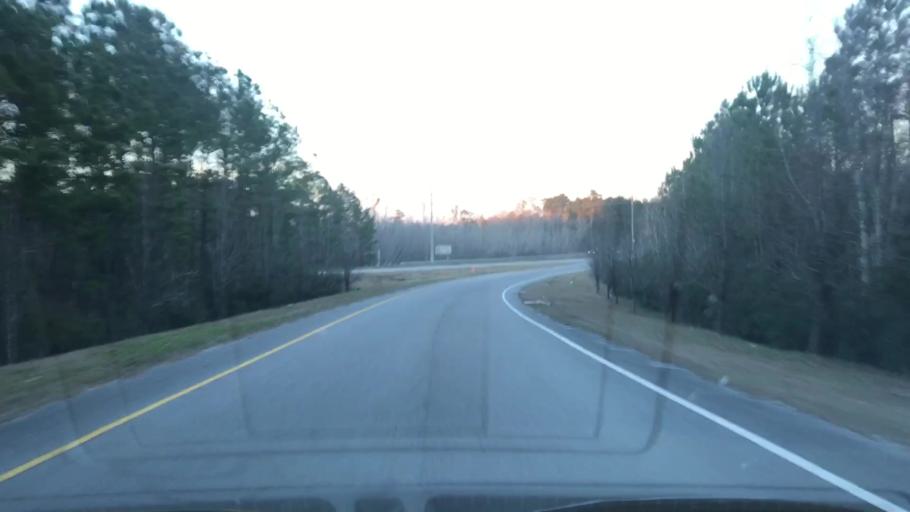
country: US
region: North Carolina
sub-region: Brunswick County
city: Shallotte
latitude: 33.9776
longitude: -78.4021
